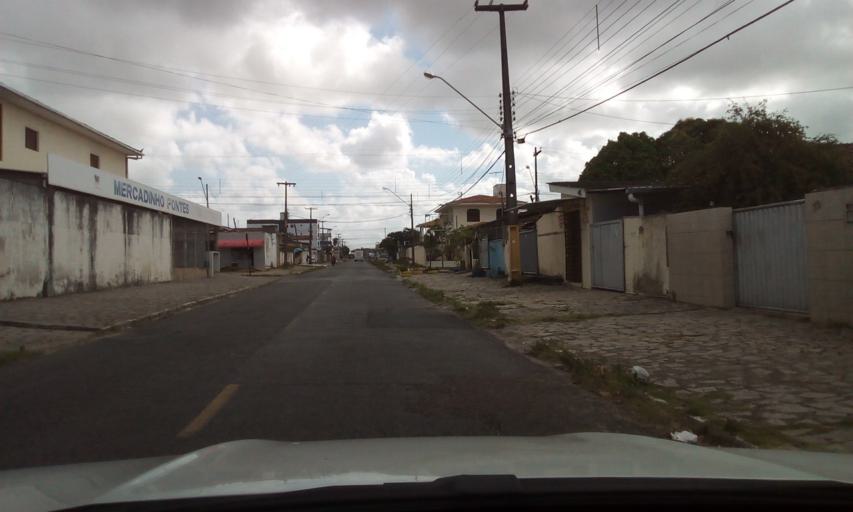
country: BR
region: Paraiba
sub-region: Joao Pessoa
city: Joao Pessoa
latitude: -7.1506
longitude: -34.8803
